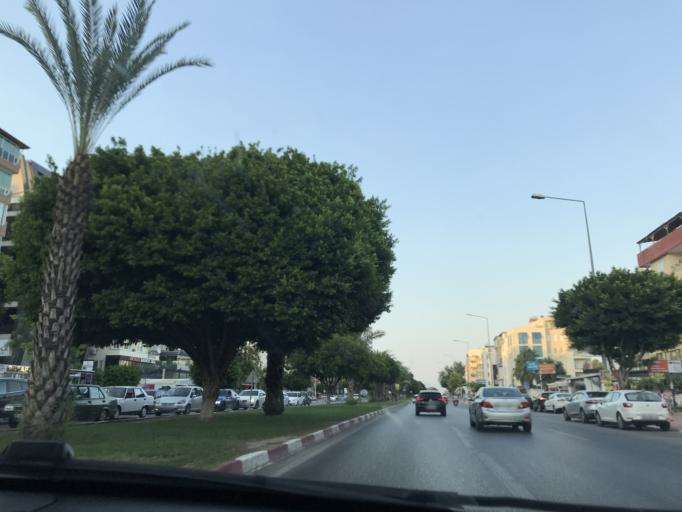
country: TR
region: Antalya
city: Antalya
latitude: 36.8660
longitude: 30.6352
